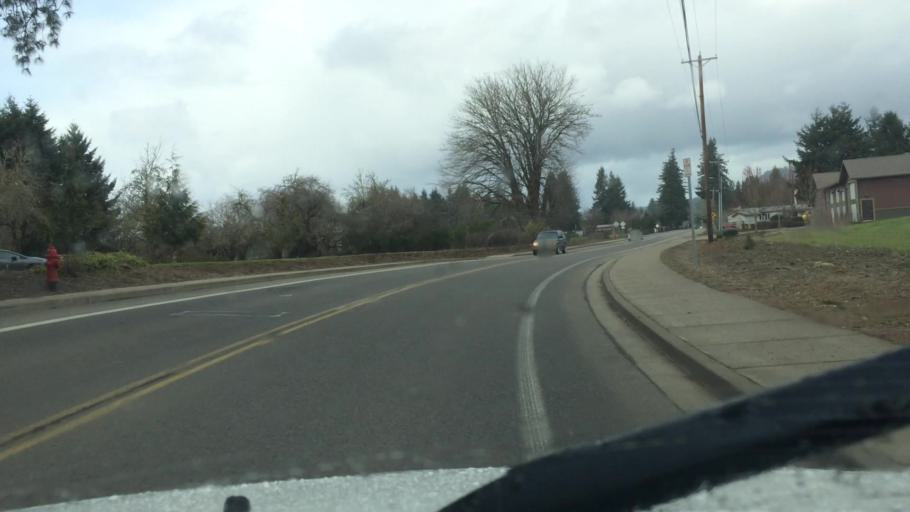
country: US
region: Oregon
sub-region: Polk County
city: Grand Ronde
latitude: 45.0657
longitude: -123.6118
